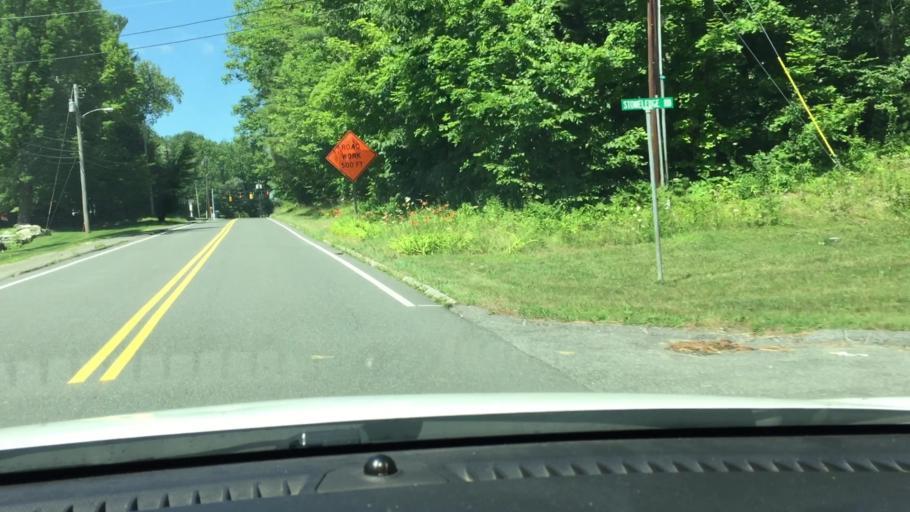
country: US
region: Massachusetts
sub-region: Berkshire County
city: Lenox
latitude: 42.3557
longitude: -73.2661
